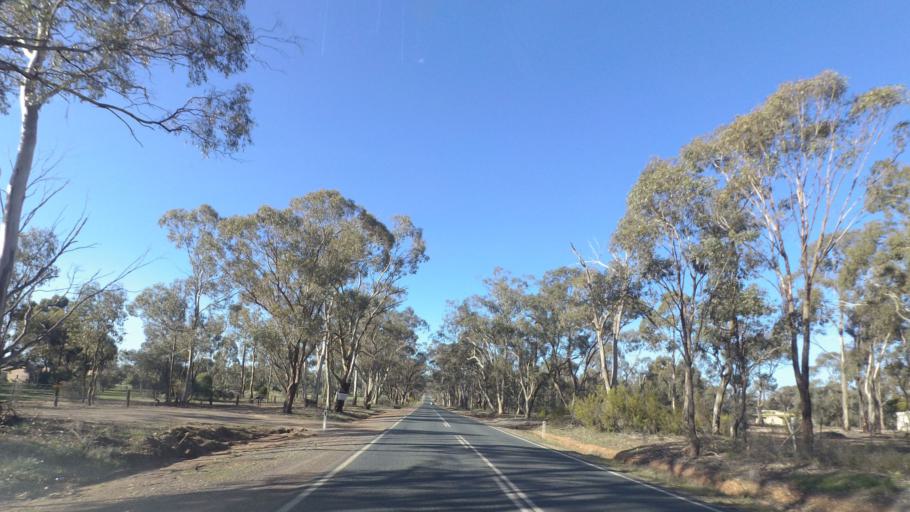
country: AU
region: Victoria
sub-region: Greater Bendigo
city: Epsom
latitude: -36.6763
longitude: 144.3911
